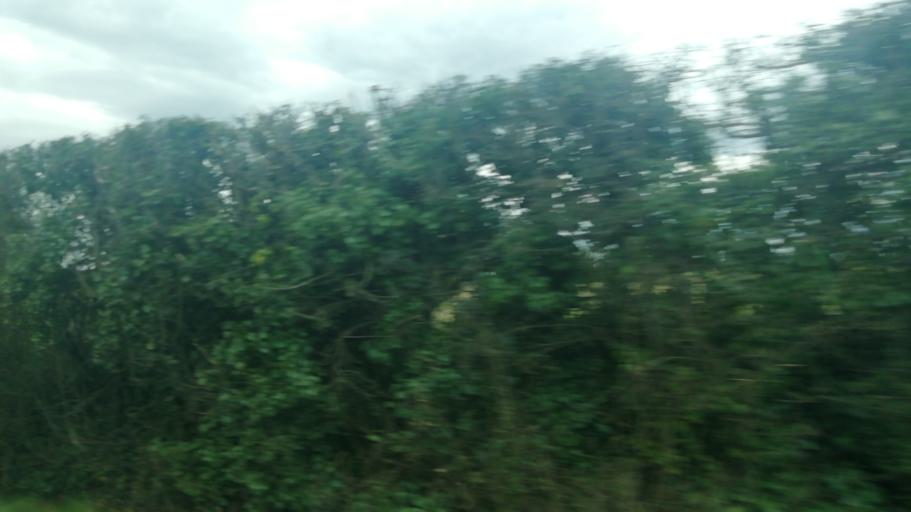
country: IE
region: Leinster
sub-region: Kildare
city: Prosperous
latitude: 53.3034
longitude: -6.7301
